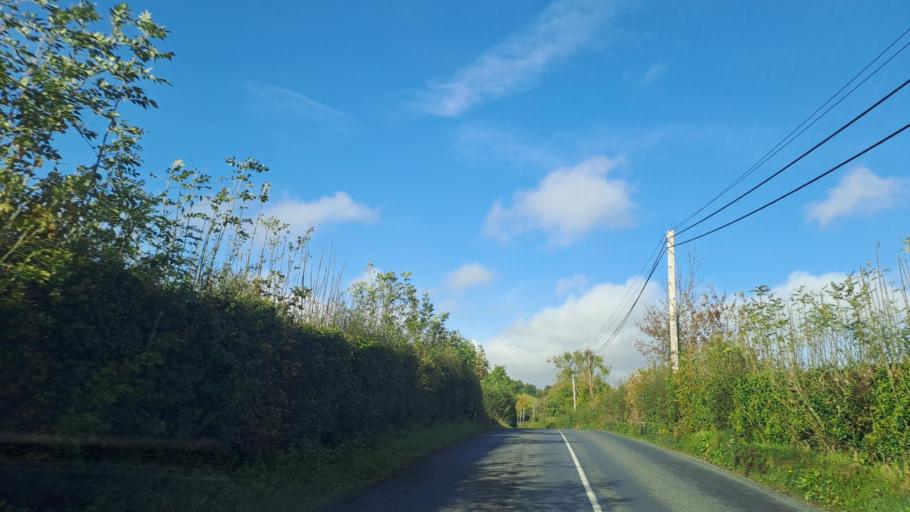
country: IE
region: Ulster
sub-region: An Cabhan
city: Bailieborough
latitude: 54.0166
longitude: -6.9320
